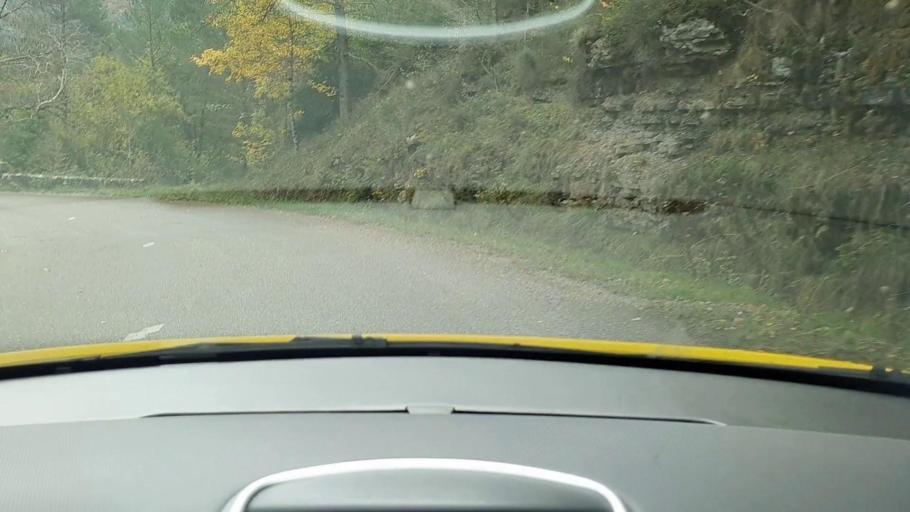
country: FR
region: Languedoc-Roussillon
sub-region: Departement de la Lozere
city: Meyrueis
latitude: 44.0769
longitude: 3.3552
